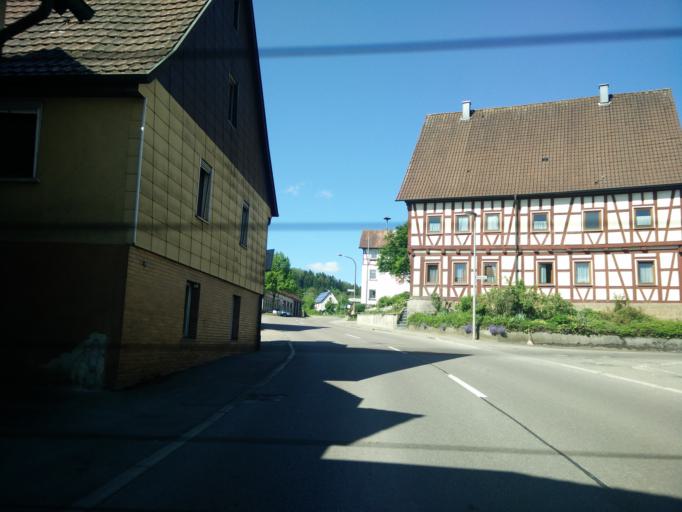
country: DE
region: Baden-Wuerttemberg
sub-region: Regierungsbezirk Stuttgart
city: Gaildorf
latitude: 48.9789
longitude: 9.7752
